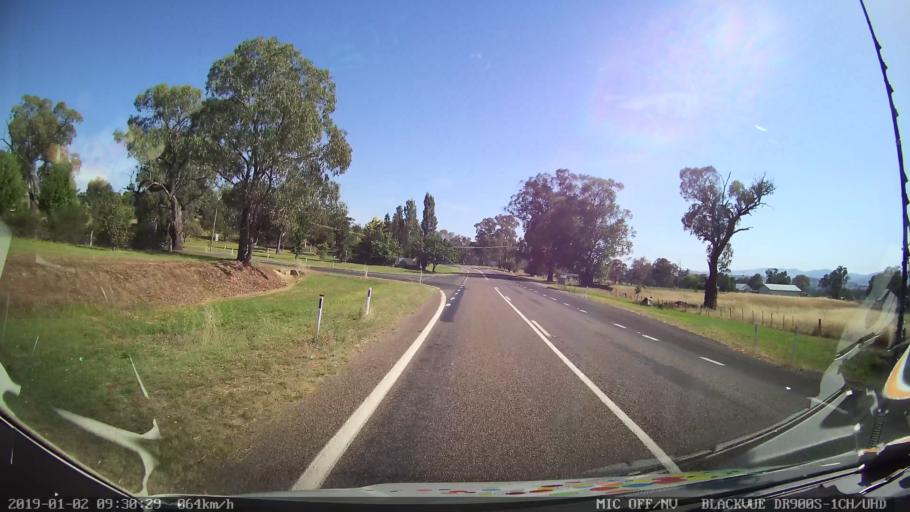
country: AU
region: New South Wales
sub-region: Tumut Shire
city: Tumut
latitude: -35.3262
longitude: 148.2378
